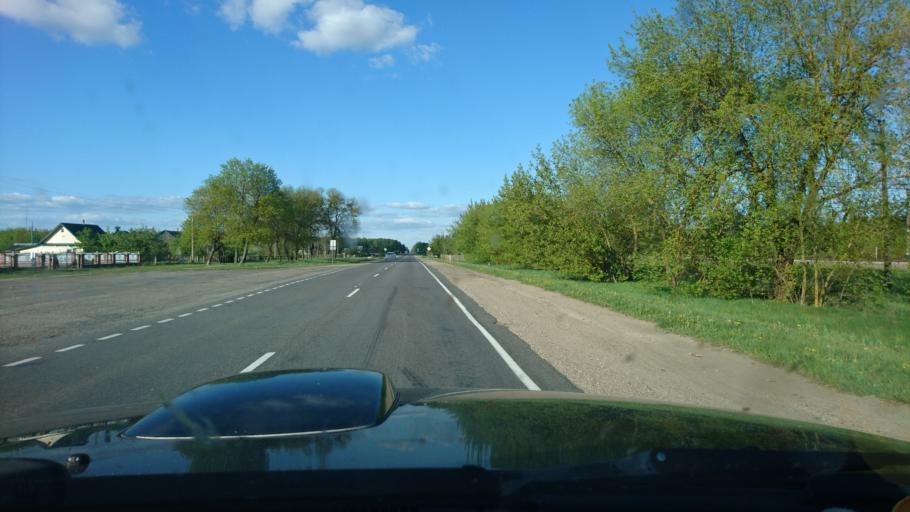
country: BY
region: Brest
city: Nyakhachava
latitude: 52.6495
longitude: 25.2166
